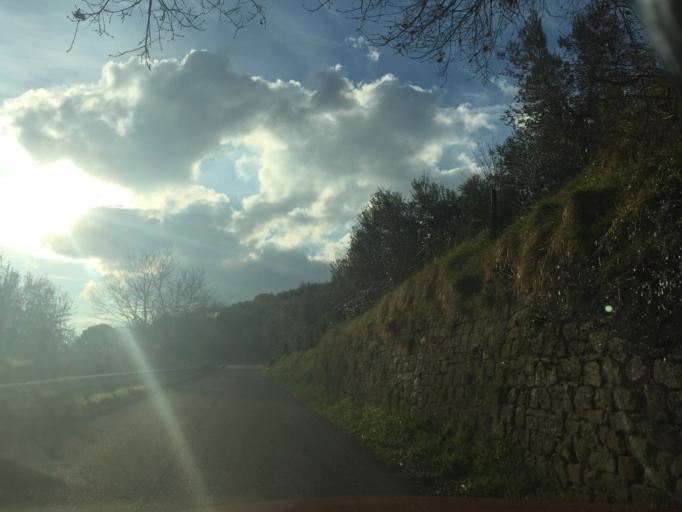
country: IT
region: Tuscany
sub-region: Province of Florence
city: Vinci
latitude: 43.8069
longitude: 10.9316
